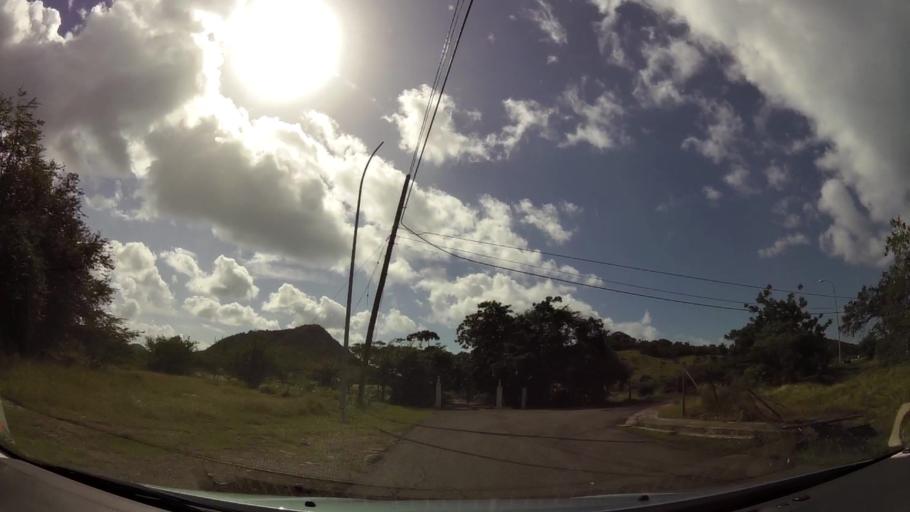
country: AG
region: Saint John
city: Saint John's
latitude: 17.1141
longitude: -61.8763
